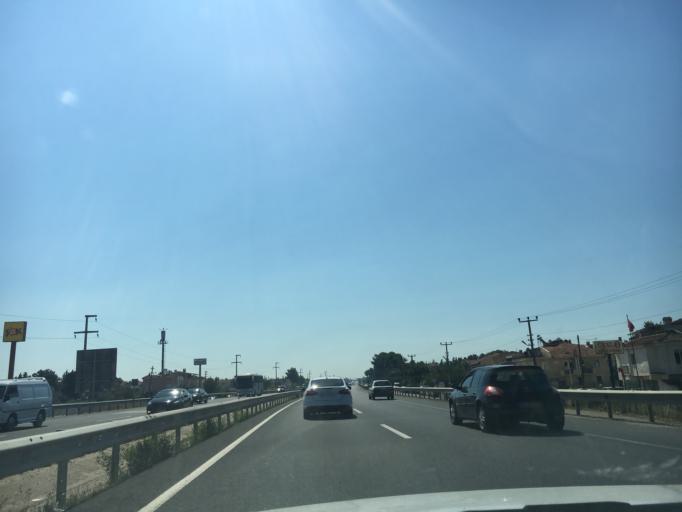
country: TR
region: Tekirdag
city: Marmara Ereglisi
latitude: 40.9929
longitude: 27.8443
